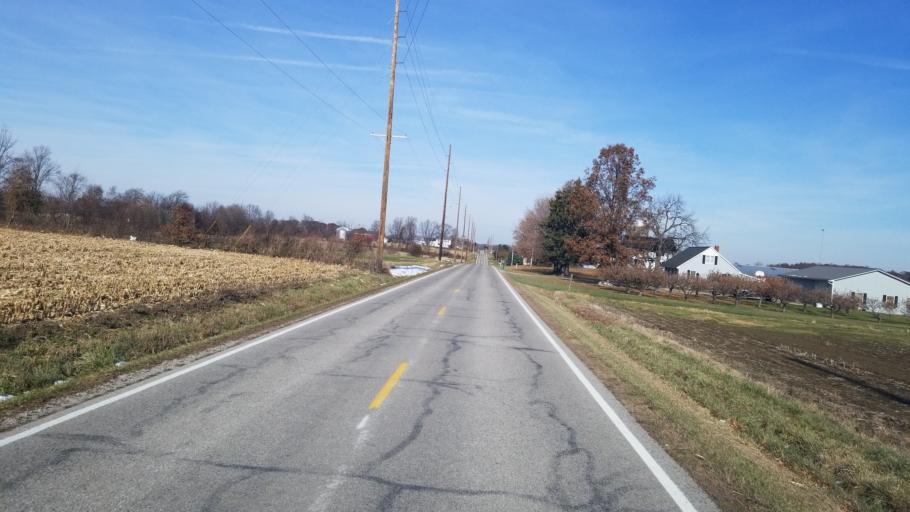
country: US
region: Ohio
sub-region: Huron County
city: Monroeville
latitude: 41.1699
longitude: -82.6838
